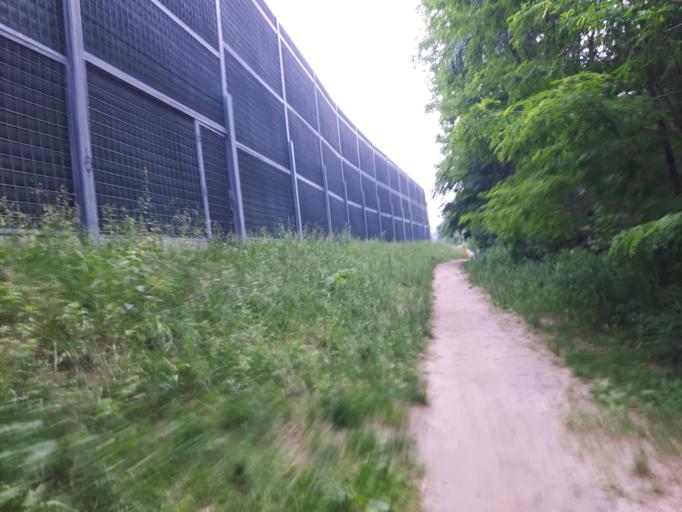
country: PL
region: Masovian Voivodeship
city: Zielonka
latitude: 52.2828
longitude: 21.1406
